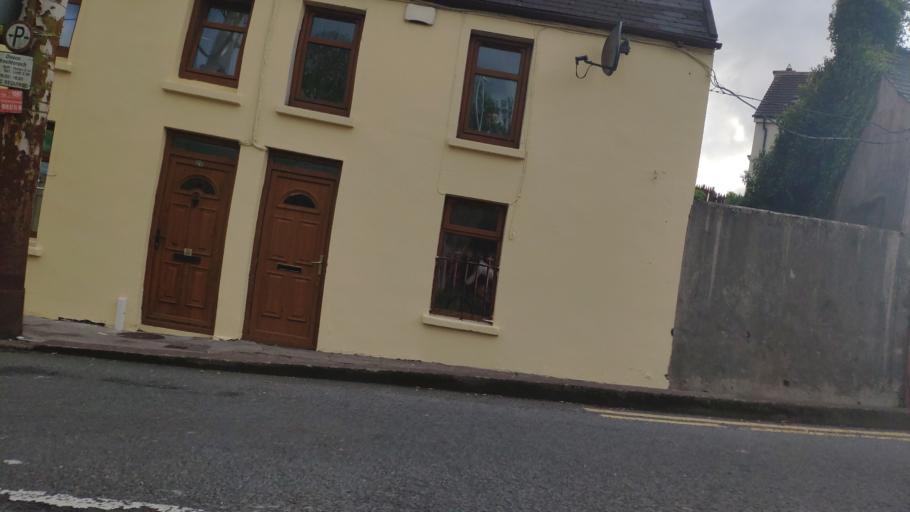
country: IE
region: Munster
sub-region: County Cork
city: Cork
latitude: 51.9064
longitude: -8.4811
